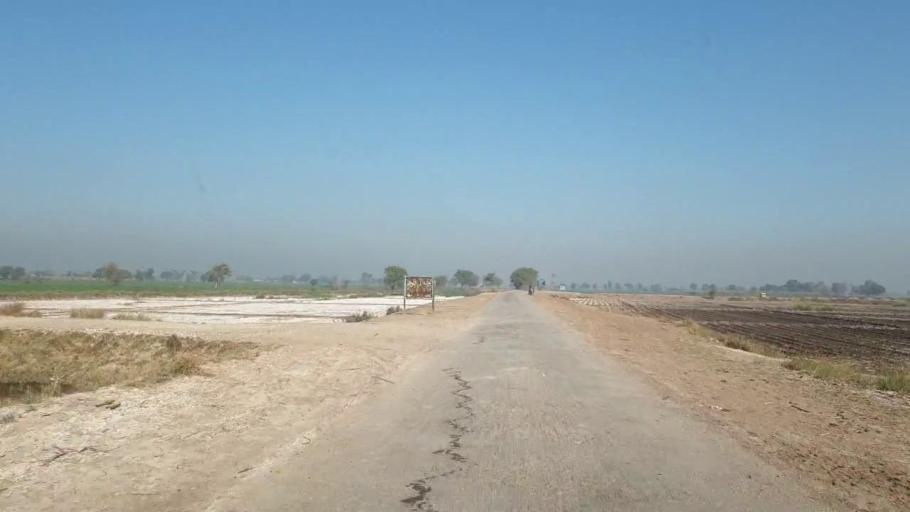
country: PK
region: Sindh
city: Shahdadpur
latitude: 25.9450
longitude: 68.5027
